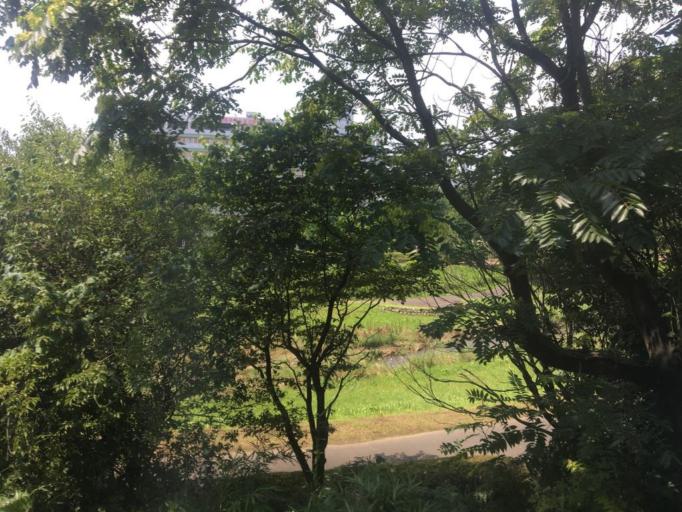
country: JP
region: Gunma
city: Maebashi-shi
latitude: 36.4061
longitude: 139.1306
